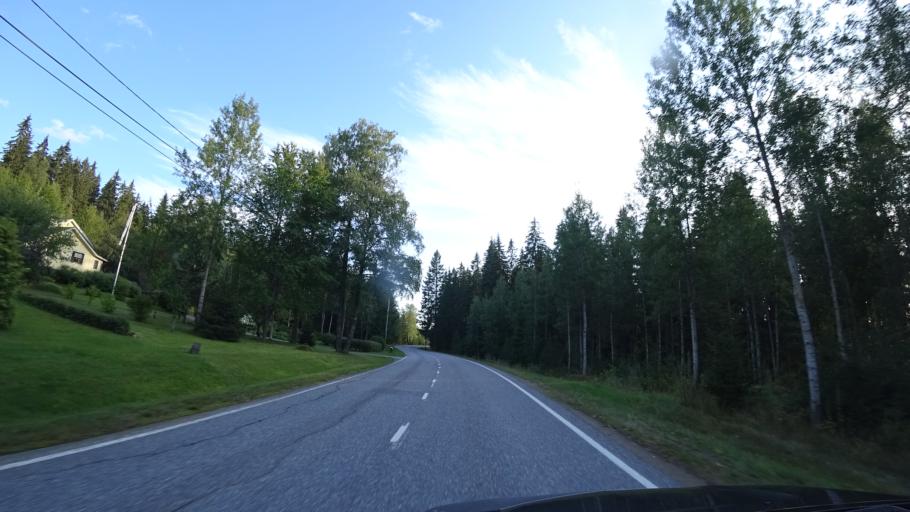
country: FI
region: Haeme
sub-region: Haemeenlinna
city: Lammi
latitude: 61.0676
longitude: 25.0026
